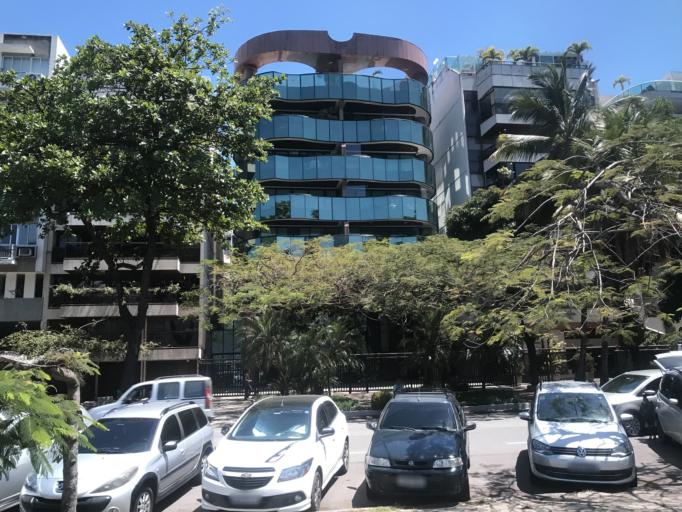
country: BR
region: Rio de Janeiro
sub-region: Rio De Janeiro
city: Rio de Janeiro
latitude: -22.9805
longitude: -43.2104
